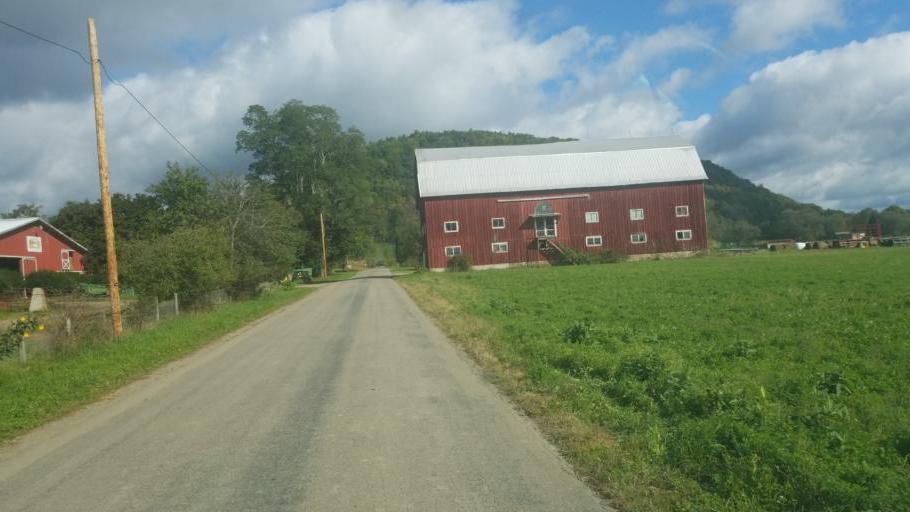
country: US
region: New York
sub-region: Cattaraugus County
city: Weston Mills
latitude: 42.1334
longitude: -78.3442
